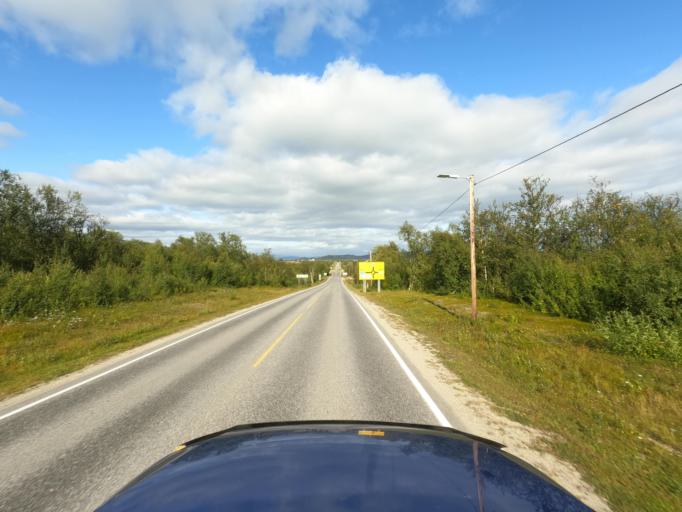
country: NO
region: Finnmark Fylke
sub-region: Porsanger
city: Lakselv
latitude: 70.0482
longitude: 24.9785
